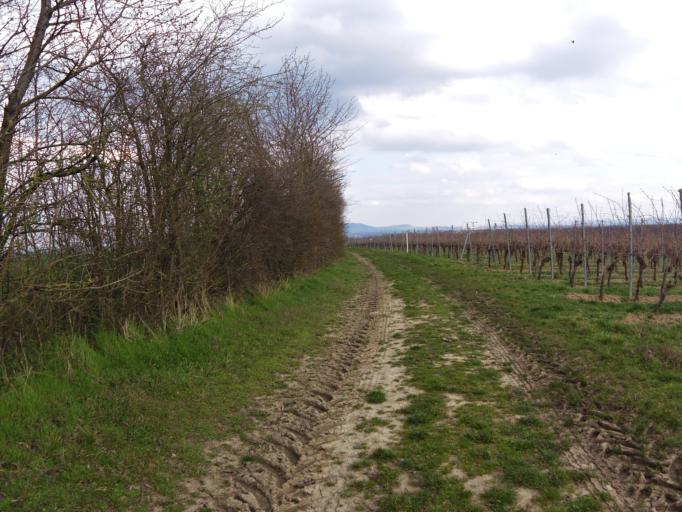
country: DE
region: Bavaria
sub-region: Regierungsbezirk Unterfranken
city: Buchbrunn
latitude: 49.7393
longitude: 10.1193
